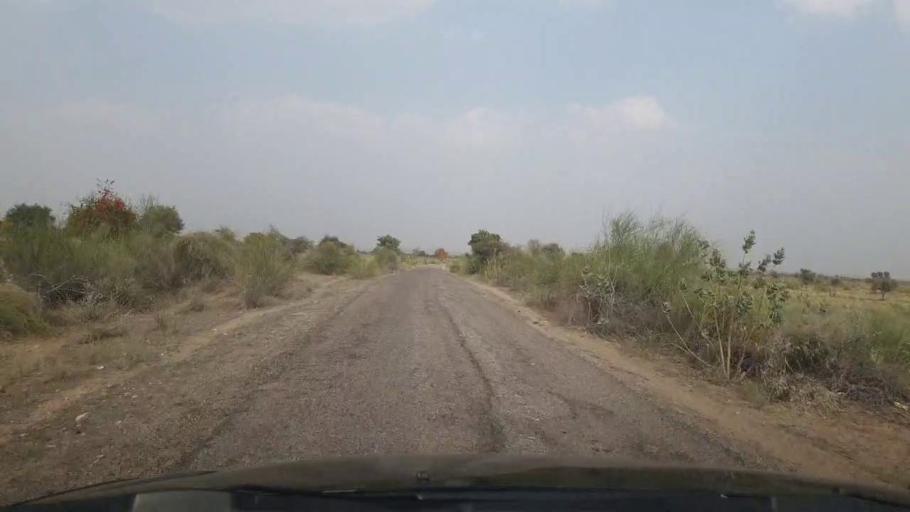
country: PK
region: Sindh
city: Islamkot
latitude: 25.0265
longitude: 70.5723
